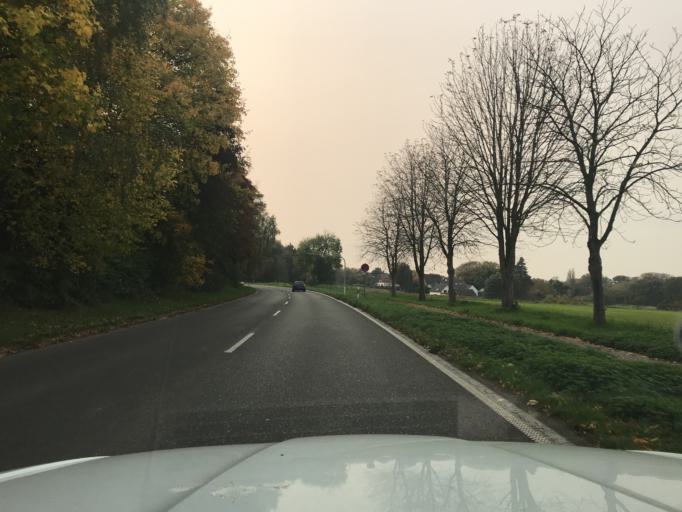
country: DE
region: North Rhine-Westphalia
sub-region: Regierungsbezirk Dusseldorf
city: Muelheim (Ruhr)
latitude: 51.4087
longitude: 6.9439
